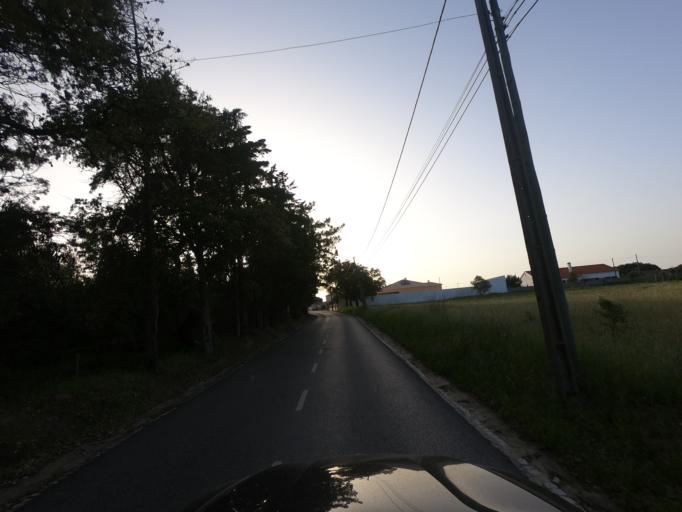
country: PT
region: Setubal
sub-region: Setubal
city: Setubal
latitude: 38.5362
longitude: -8.8209
